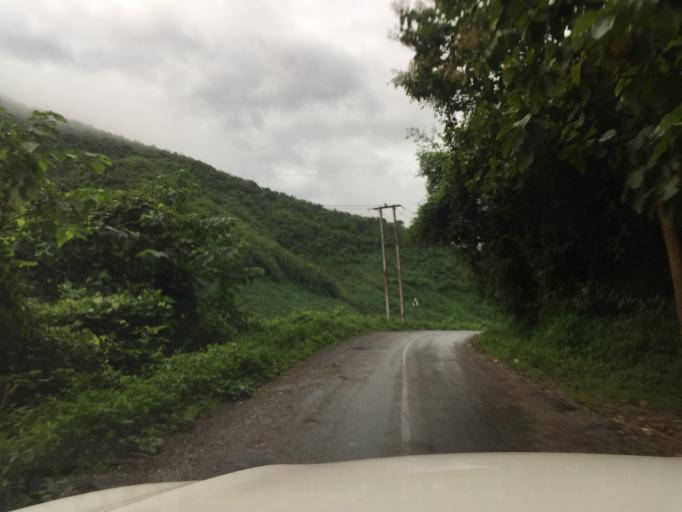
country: LA
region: Oudomxai
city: Muang La
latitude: 21.0384
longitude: 102.2399
